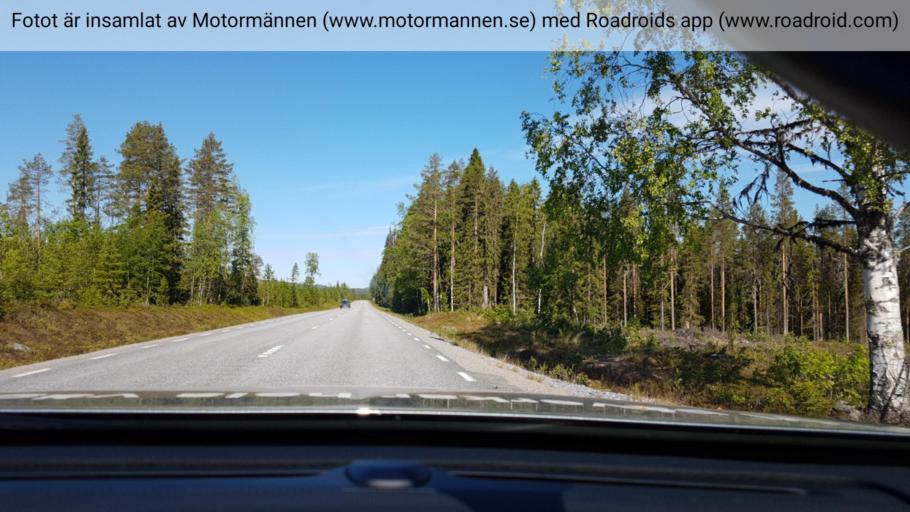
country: SE
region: Vaesterbotten
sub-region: Bjurholms Kommun
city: Bjurholm
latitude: 63.9564
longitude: 18.8740
